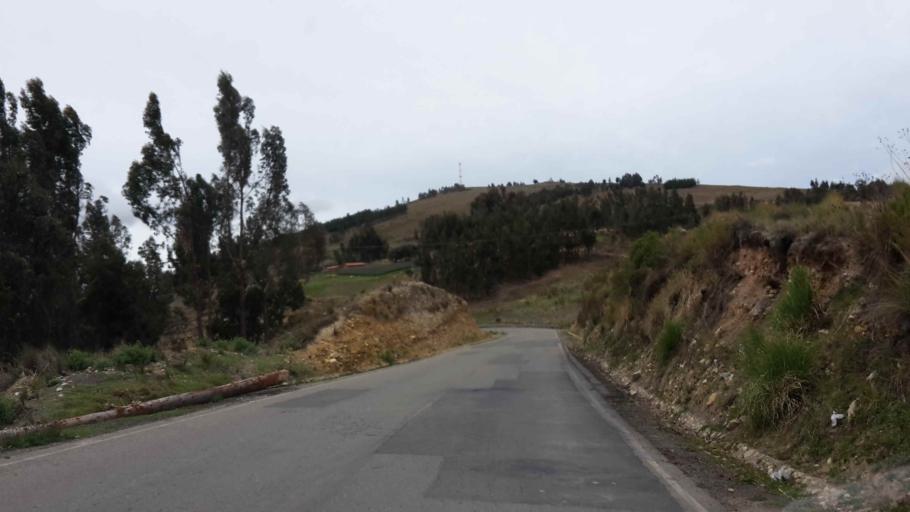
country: BO
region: Cochabamba
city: Arani
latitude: -17.4791
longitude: -65.6225
